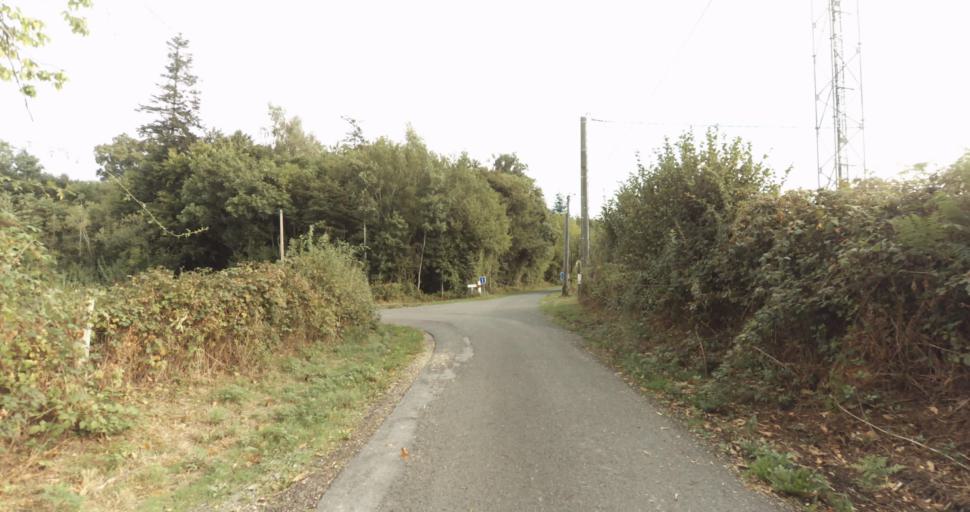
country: FR
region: Lower Normandy
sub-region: Departement de l'Orne
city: Vimoutiers
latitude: 48.8364
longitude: 0.2100
